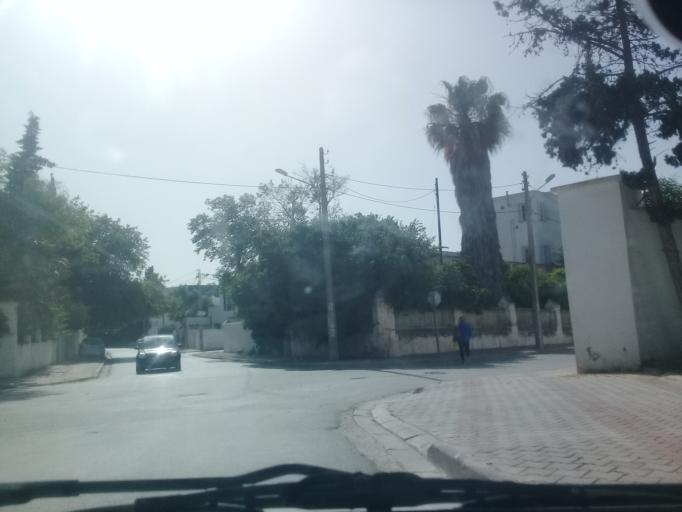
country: TN
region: Tunis
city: Al Marsa
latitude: 36.8837
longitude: 10.3262
